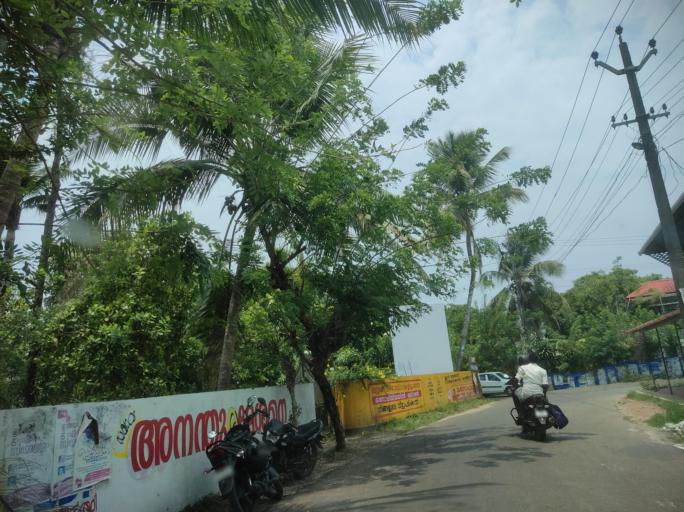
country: IN
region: Kerala
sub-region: Alappuzha
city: Kutiatodu
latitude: 9.7513
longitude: 76.3252
